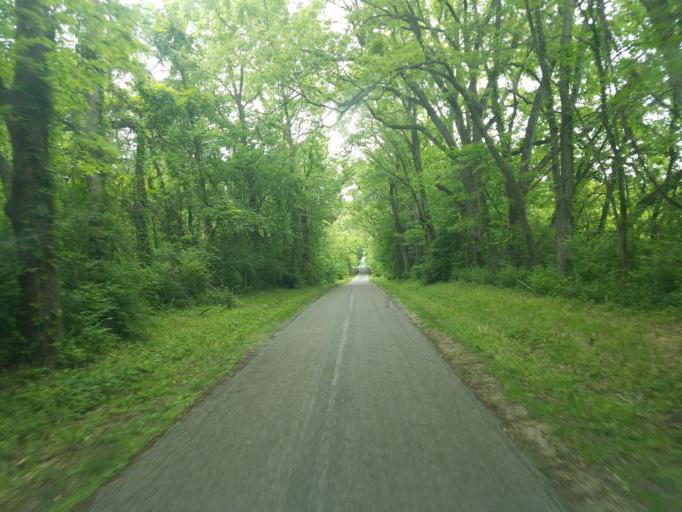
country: US
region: Ohio
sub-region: Morrow County
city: Cardington
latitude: 40.5317
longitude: -83.0144
